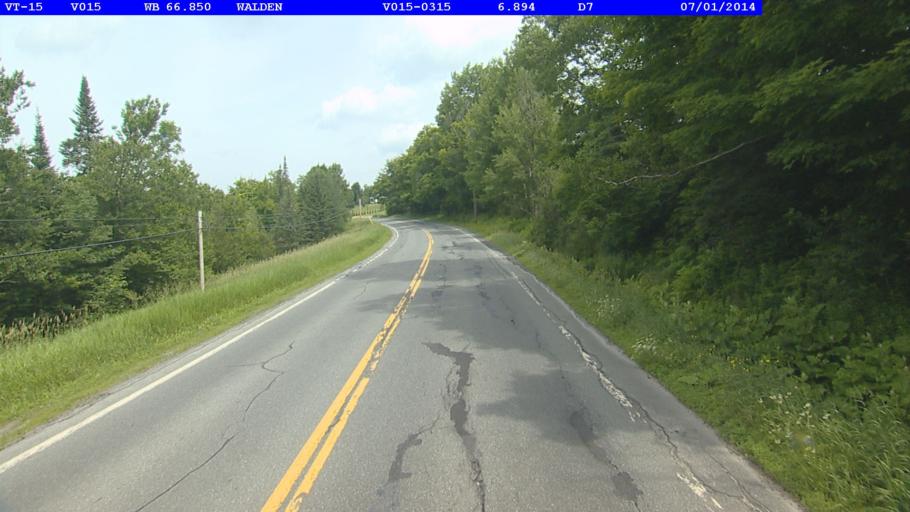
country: US
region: Vermont
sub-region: Caledonia County
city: Hardwick
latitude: 44.4266
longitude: -72.2190
